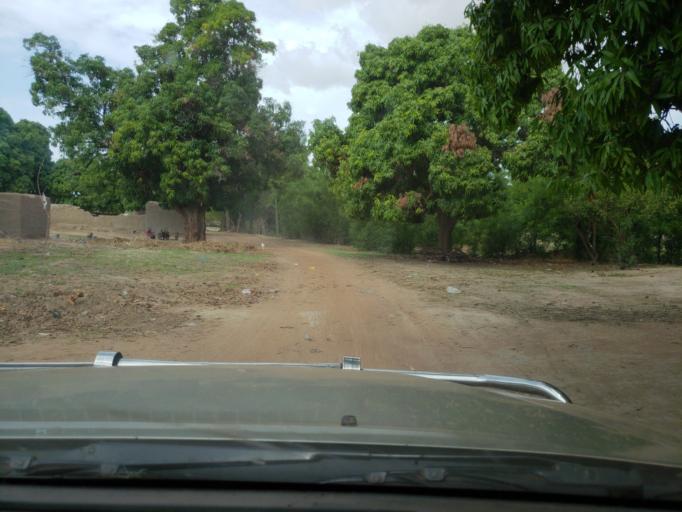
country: ML
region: Segou
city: Bla
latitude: 12.7341
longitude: -5.6677
